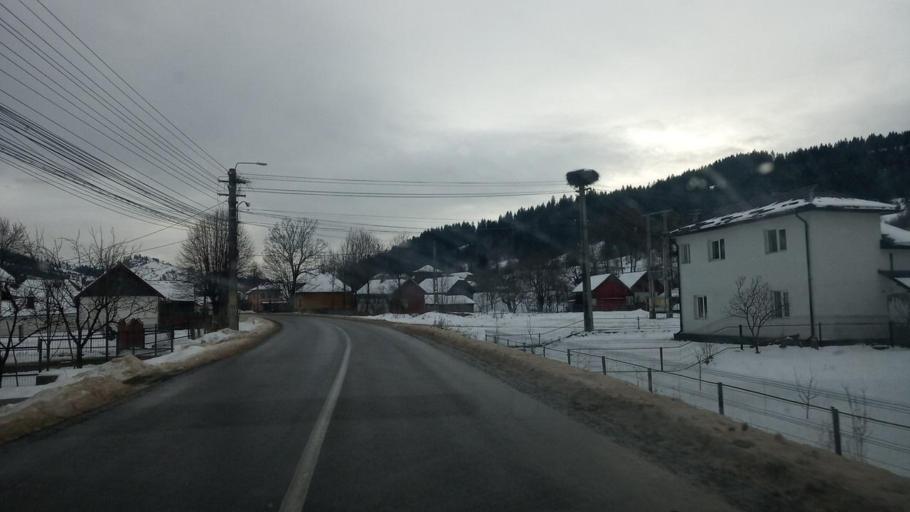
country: RO
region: Suceava
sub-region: Comuna Frasin
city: Frasin
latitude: 47.5222
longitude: 25.7974
